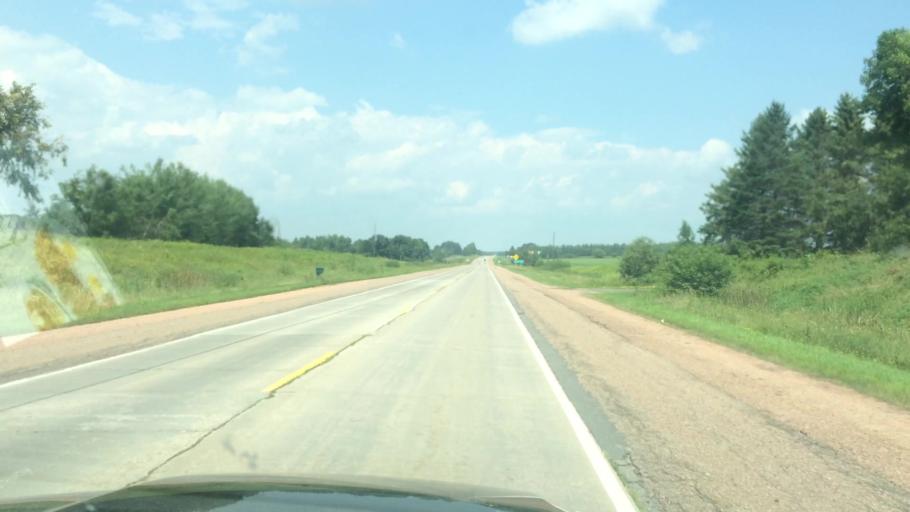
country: US
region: Wisconsin
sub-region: Clark County
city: Colby
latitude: 44.8698
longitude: -90.3157
